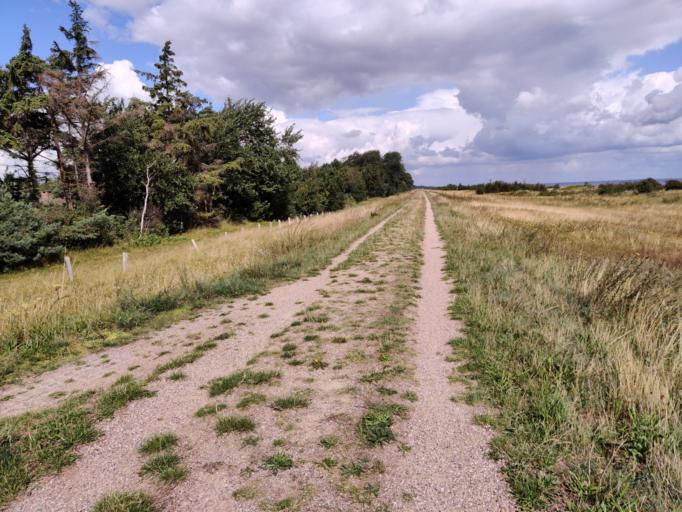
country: DK
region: Zealand
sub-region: Guldborgsund Kommune
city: Nykobing Falster
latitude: 54.5981
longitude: 11.9684
